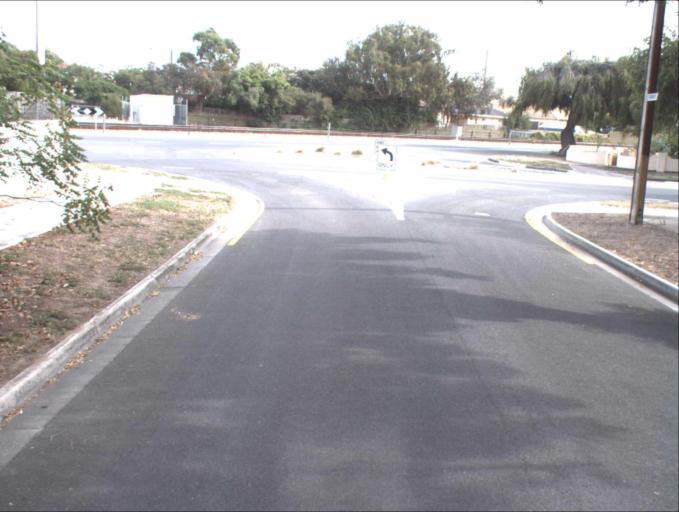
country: AU
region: South Australia
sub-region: Port Adelaide Enfield
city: Birkenhead
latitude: -34.8228
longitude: 138.4924
